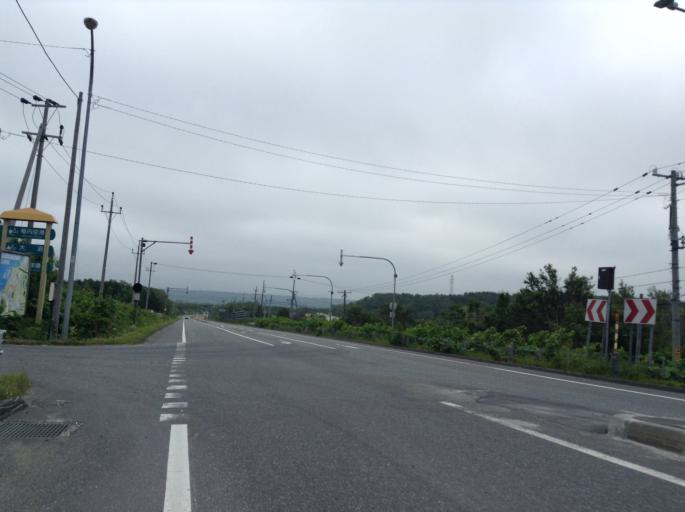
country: JP
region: Hokkaido
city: Wakkanai
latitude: 45.3718
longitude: 141.7204
